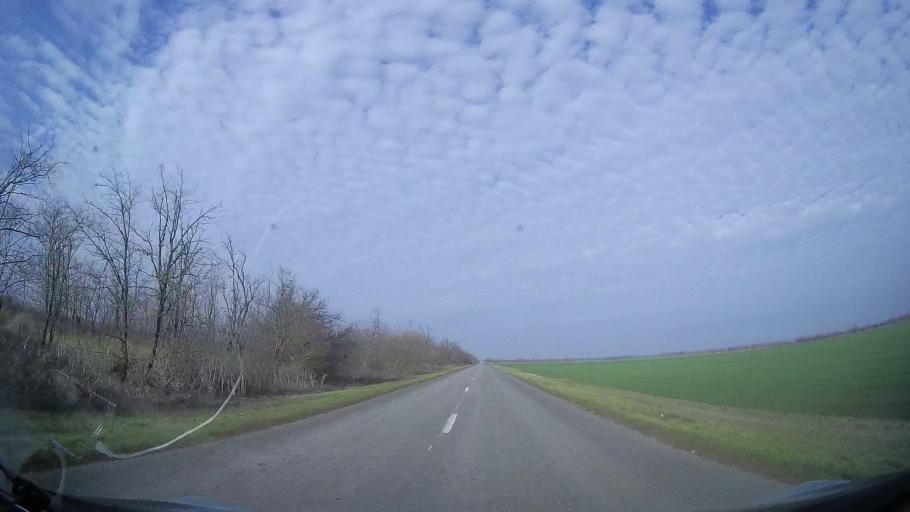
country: RU
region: Rostov
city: Gigant
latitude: 46.8665
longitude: 41.2768
